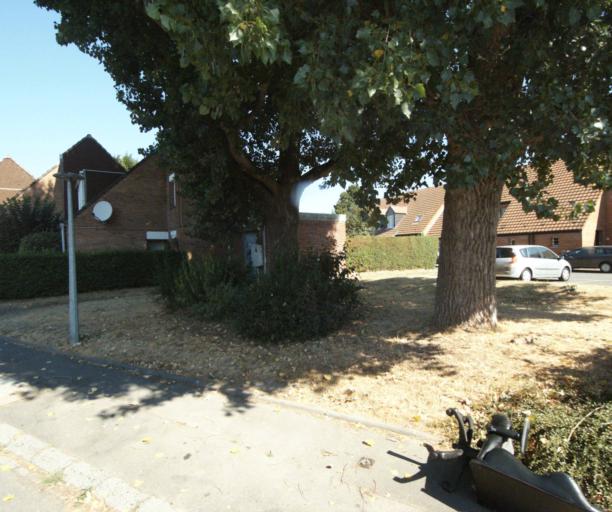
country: FR
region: Nord-Pas-de-Calais
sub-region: Departement du Nord
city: Wattrelos
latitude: 50.7047
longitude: 3.2084
